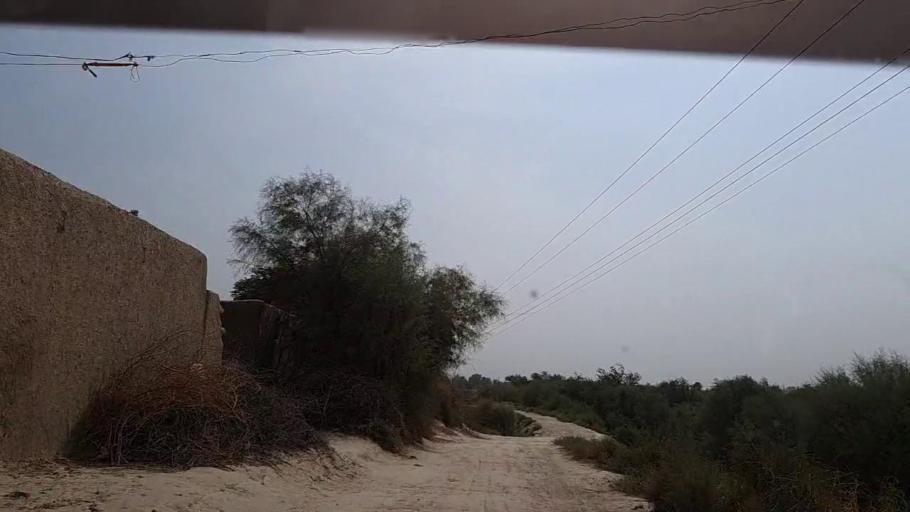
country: PK
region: Sindh
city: Khairpur Nathan Shah
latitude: 27.0268
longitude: 67.6744
